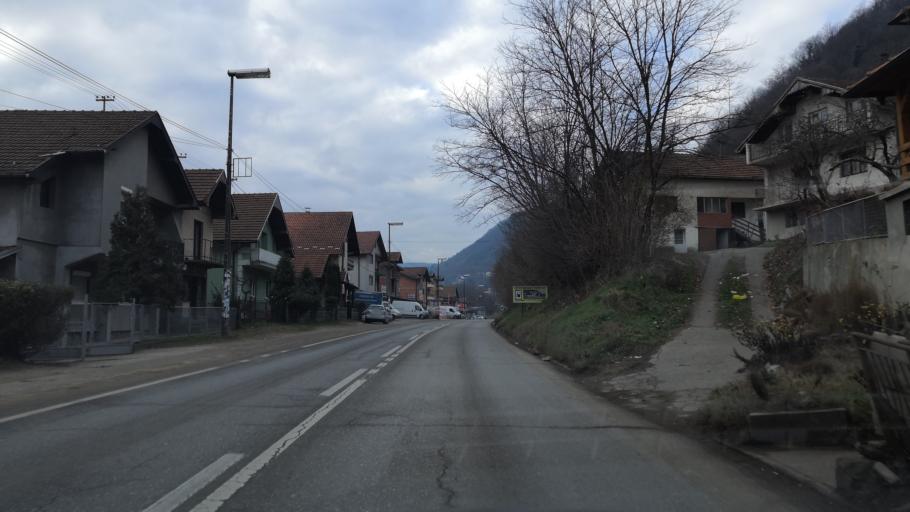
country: BA
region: Republika Srpska
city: Zvornik
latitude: 44.4020
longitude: 19.1147
